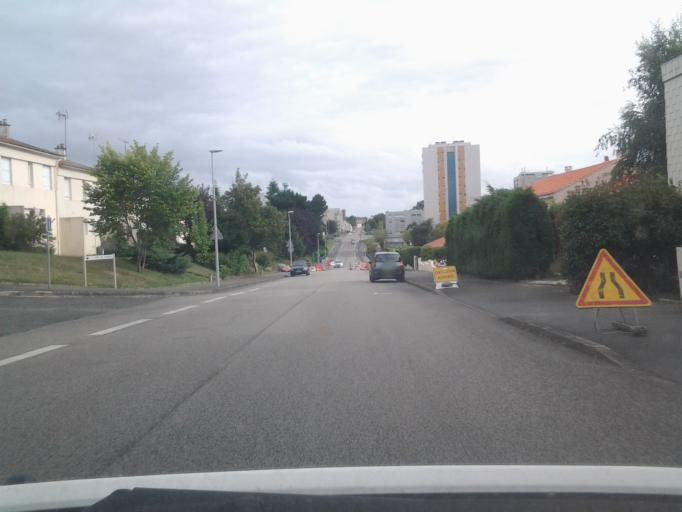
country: FR
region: Pays de la Loire
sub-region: Departement de la Vendee
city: La Roche-sur-Yon
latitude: 46.6827
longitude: -1.4222
